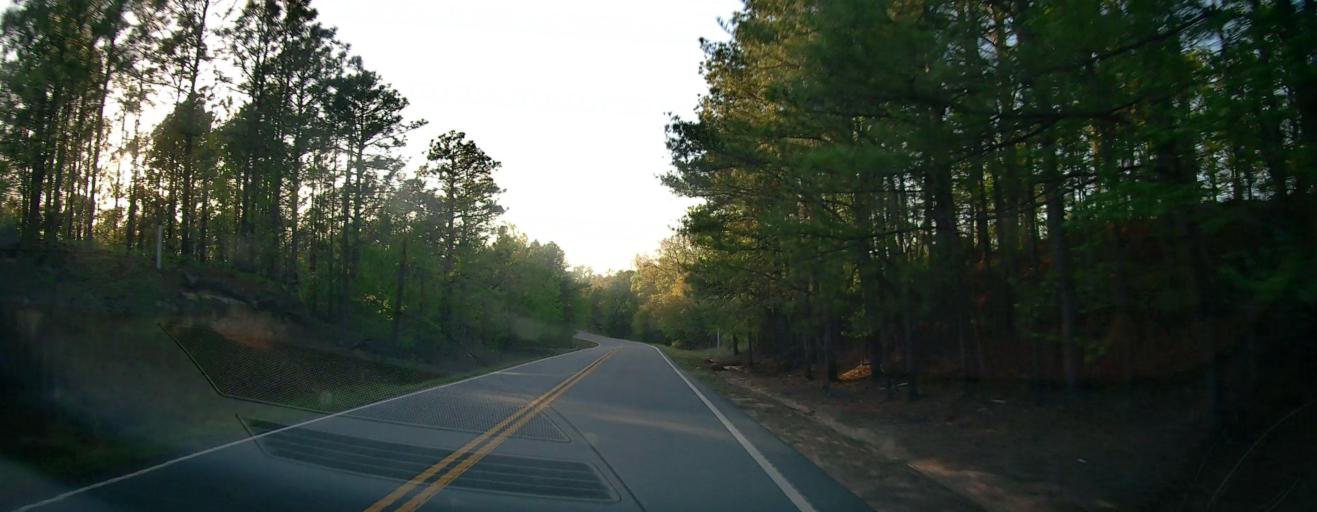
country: US
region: Georgia
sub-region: Talbot County
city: Talbotton
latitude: 32.5295
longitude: -84.4814
